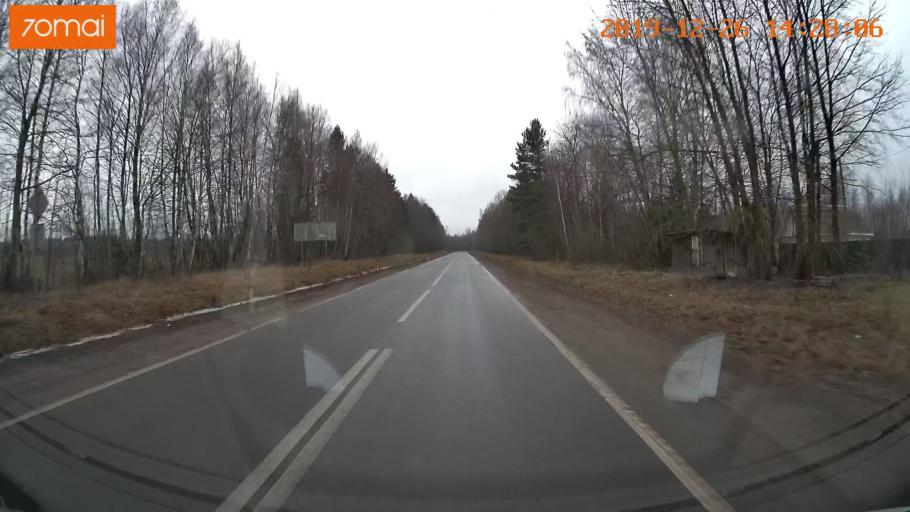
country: RU
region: Jaroslavl
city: Poshekhon'ye
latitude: 58.4791
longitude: 39.0570
